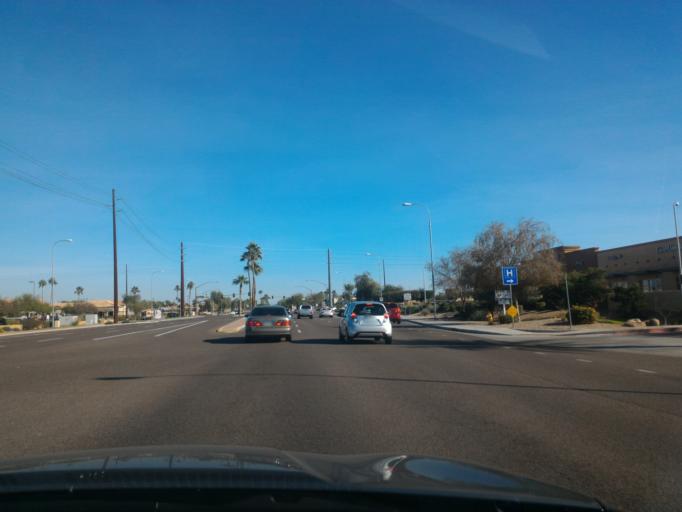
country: US
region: Arizona
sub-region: Maricopa County
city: Chandler
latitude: 33.3059
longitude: -111.8787
